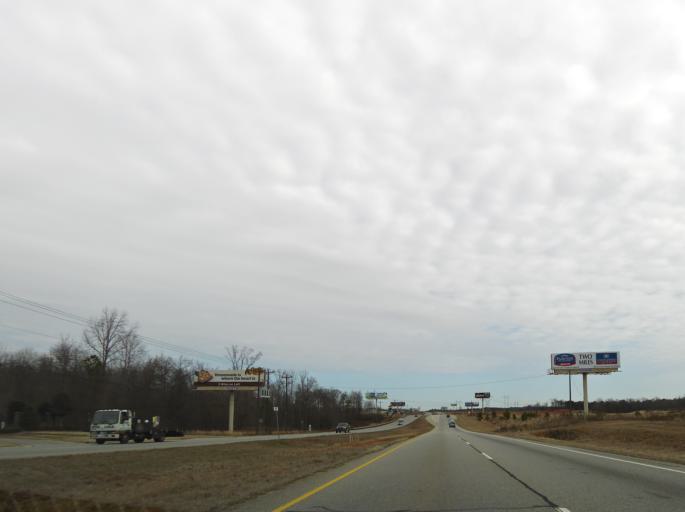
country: US
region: Georgia
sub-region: Houston County
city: Centerville
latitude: 32.6149
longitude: -83.7293
